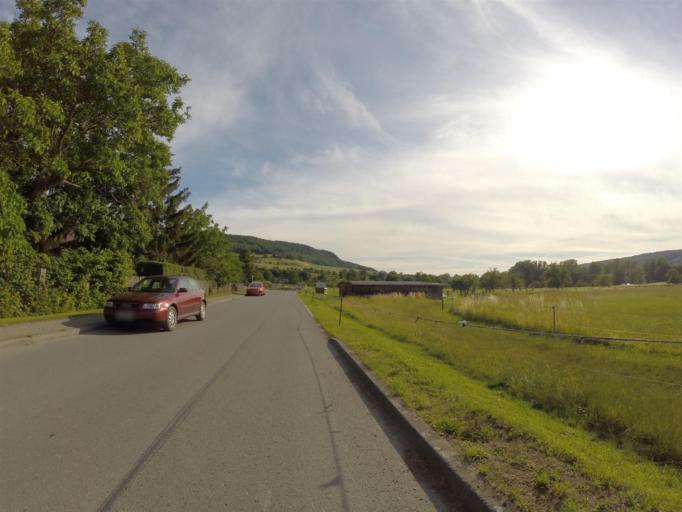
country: DE
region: Thuringia
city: Golmsdorf
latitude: 50.9741
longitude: 11.6671
